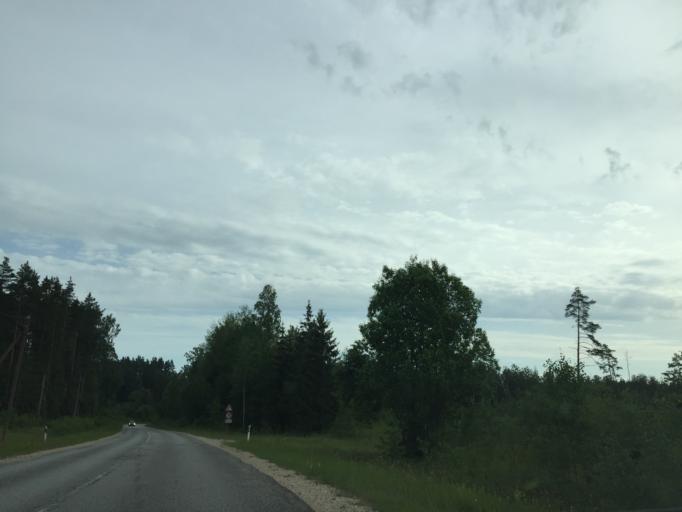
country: LV
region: Tukuma Rajons
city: Tukums
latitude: 57.0312
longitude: 23.1656
